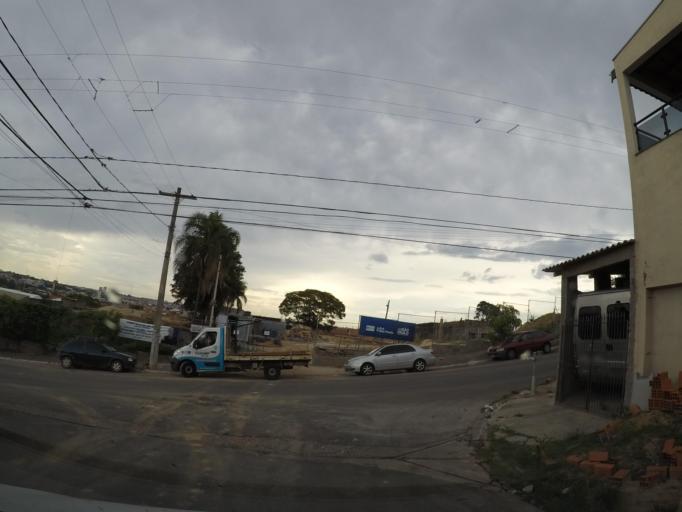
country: BR
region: Sao Paulo
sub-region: Sumare
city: Sumare
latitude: -22.8148
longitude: -47.2506
